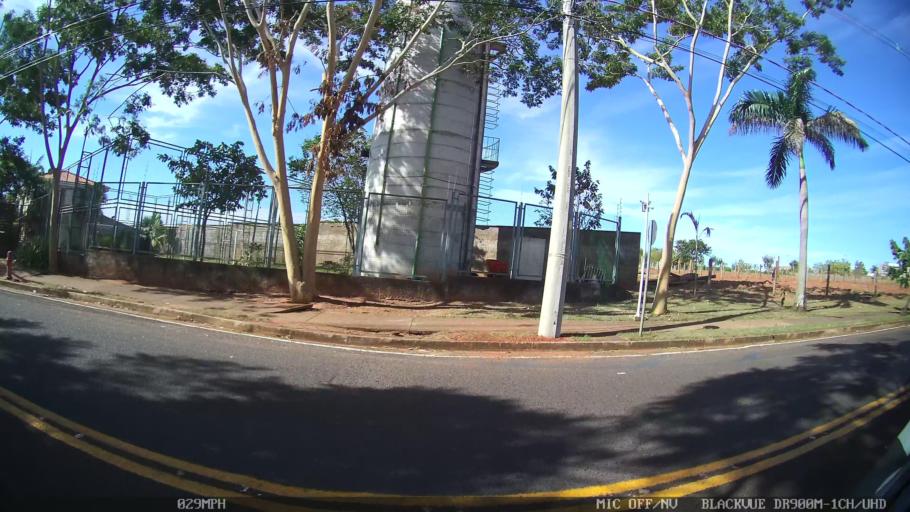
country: BR
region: Sao Paulo
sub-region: Sao Jose Do Rio Preto
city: Sao Jose do Rio Preto
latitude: -20.8054
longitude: -49.3317
